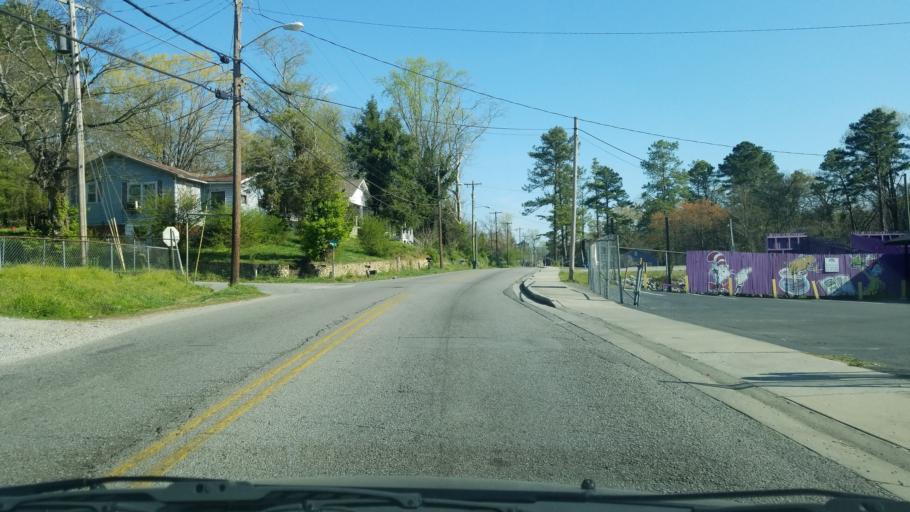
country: US
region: Tennessee
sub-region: Hamilton County
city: East Ridge
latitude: 35.0389
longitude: -85.2400
